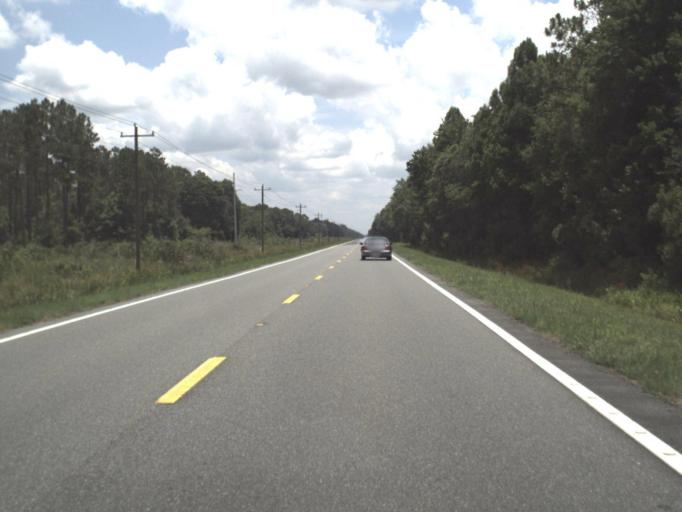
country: US
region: Florida
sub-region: Levy County
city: Chiefland
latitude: 29.2547
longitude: -82.8985
